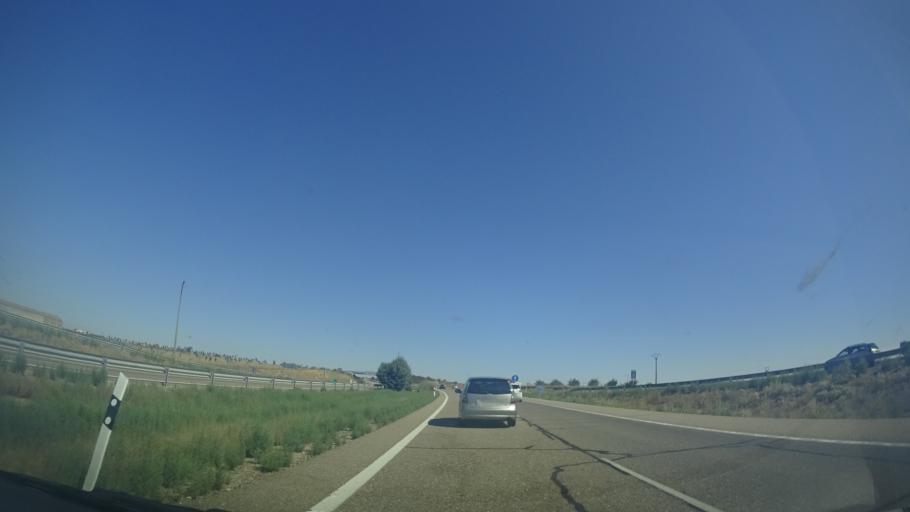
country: ES
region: Castille and Leon
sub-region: Provincia de Zamora
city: Villalpando
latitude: 41.8559
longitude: -5.4207
